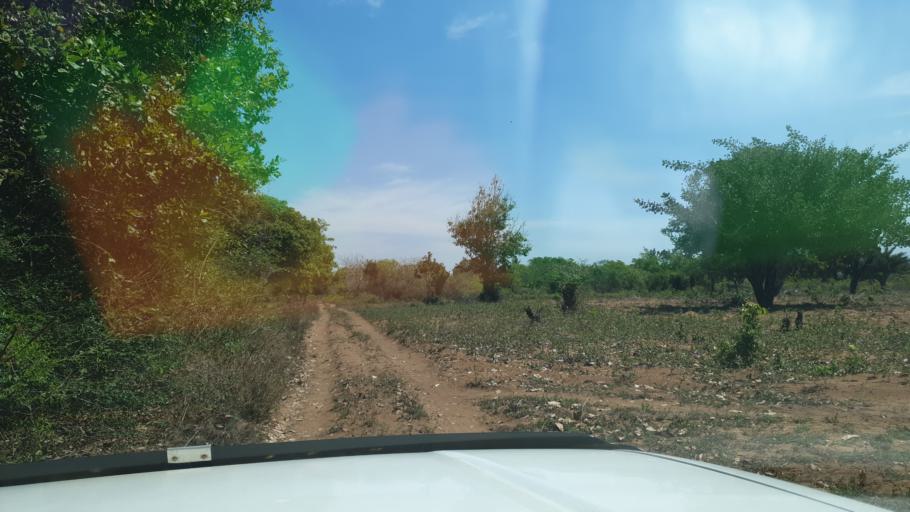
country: MZ
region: Gaza
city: Manjacaze
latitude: -24.8795
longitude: 33.9366
